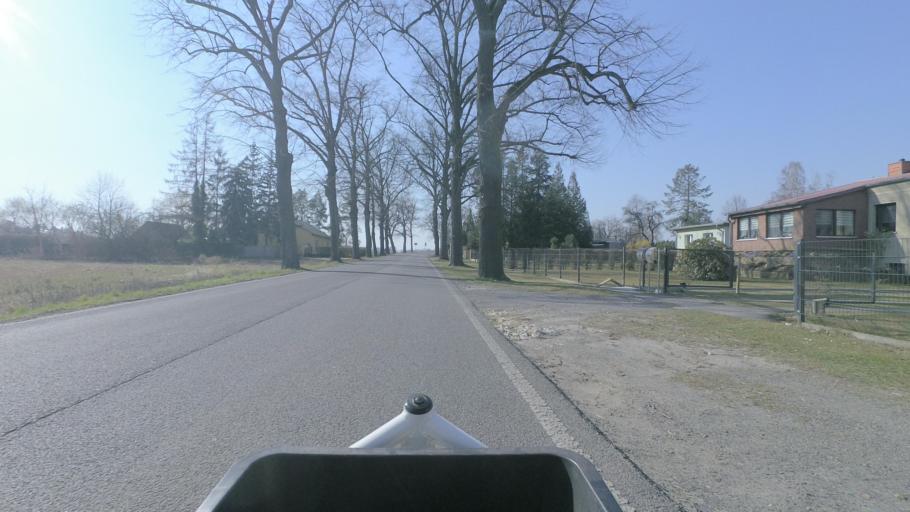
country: DE
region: Brandenburg
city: Am Mellensee
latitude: 52.1865
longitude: 13.3968
